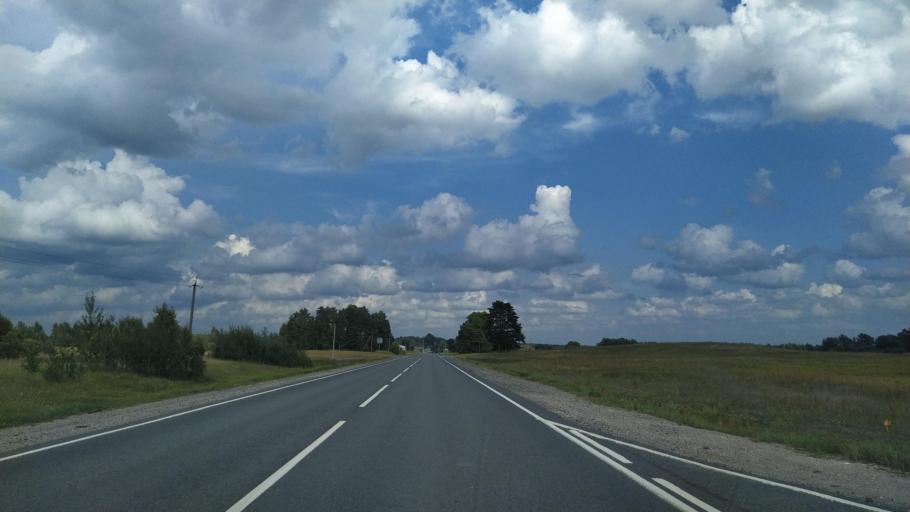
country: RU
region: Novgorod
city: Sol'tsy
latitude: 58.0987
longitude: 30.1865
